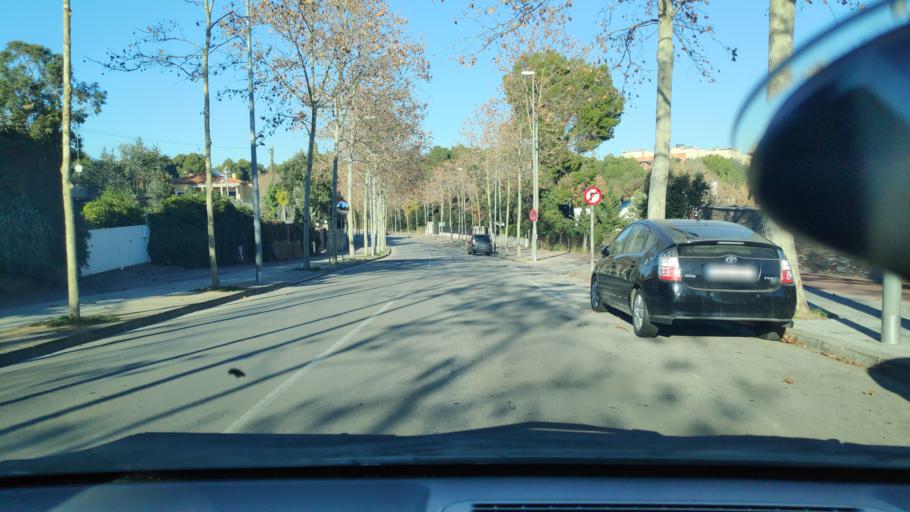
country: ES
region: Catalonia
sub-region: Provincia de Barcelona
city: Sant Quirze del Valles
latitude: 41.5593
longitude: 2.0747
